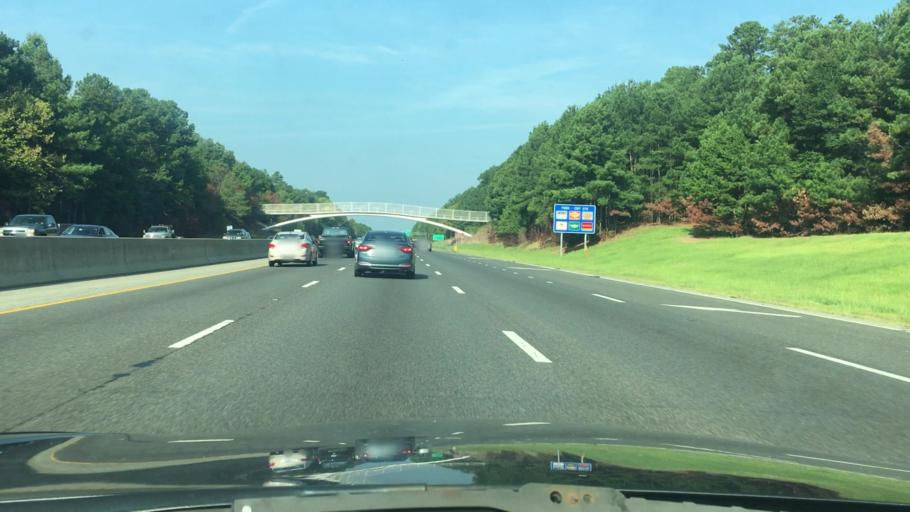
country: US
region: North Carolina
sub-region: Durham County
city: Durham
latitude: 35.9083
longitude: -78.9407
